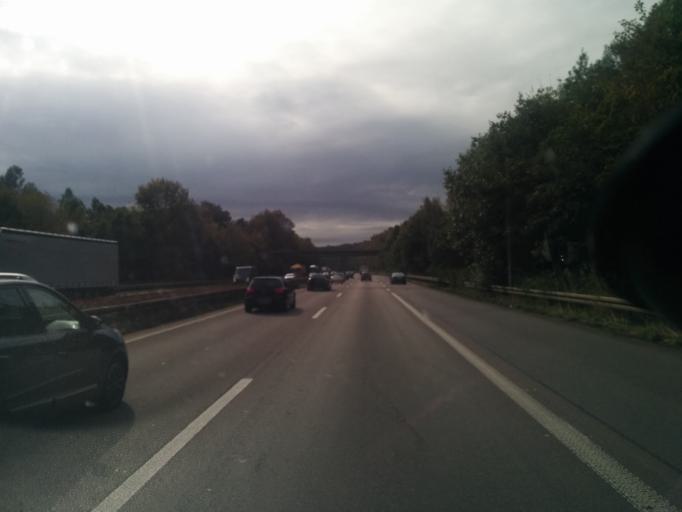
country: DE
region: North Rhine-Westphalia
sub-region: Regierungsbezirk Koln
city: Frechen
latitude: 50.8893
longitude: 6.8162
